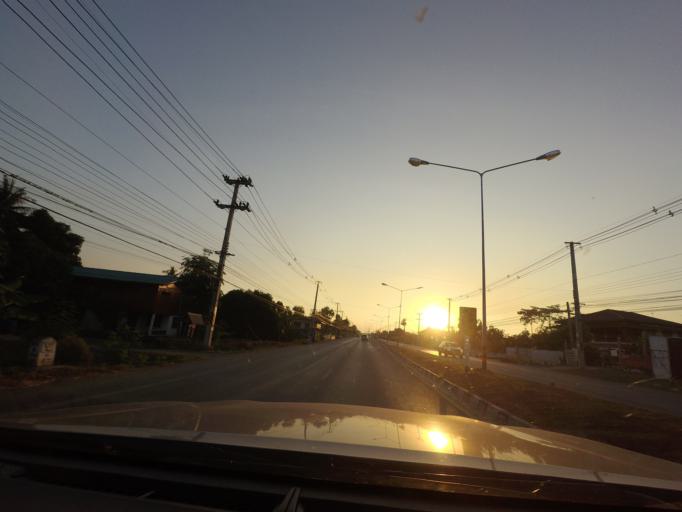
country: TH
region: Sukhothai
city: Sukhothai
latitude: 17.0553
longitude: 99.8315
